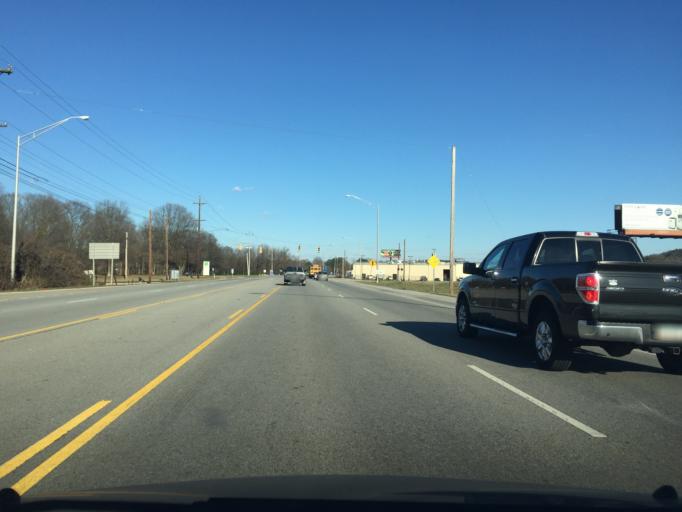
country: US
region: Tennessee
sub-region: Hamilton County
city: East Chattanooga
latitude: 35.0956
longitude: -85.2463
